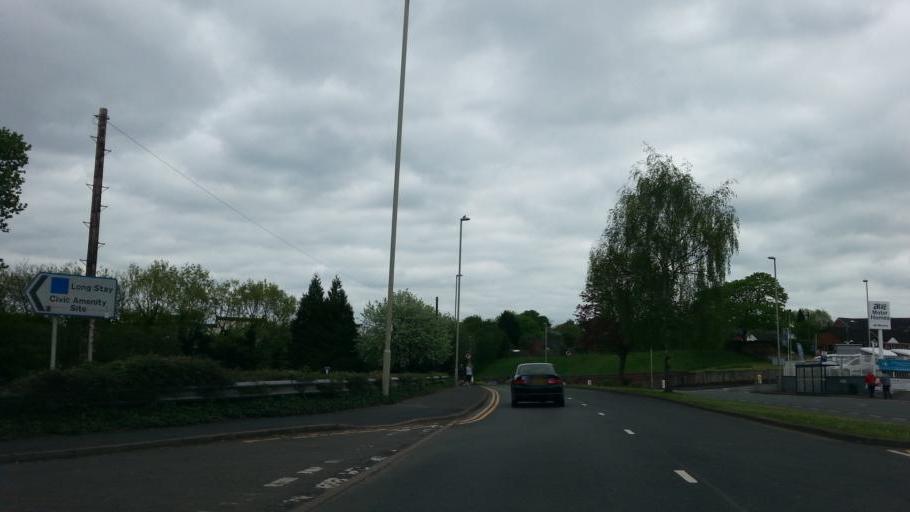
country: GB
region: England
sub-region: Dudley
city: Stourbridge
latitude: 52.4576
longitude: -2.1435
